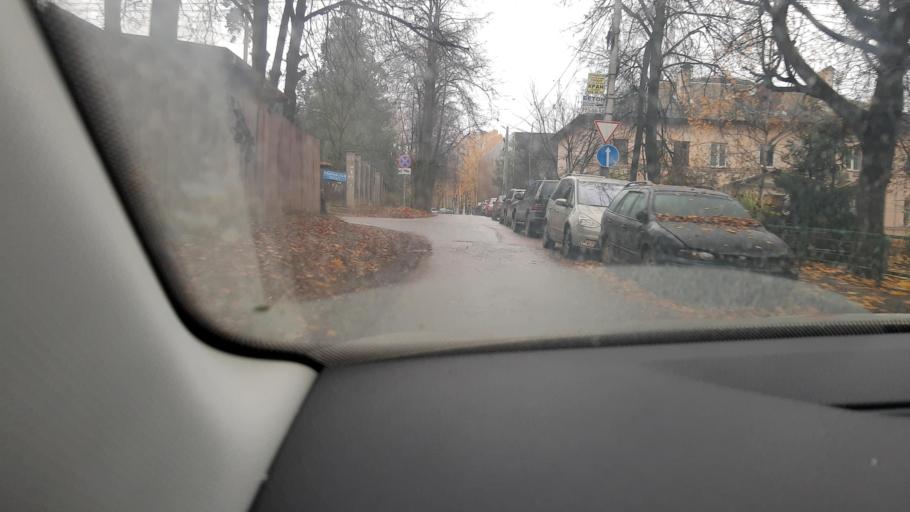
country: RU
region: Moskovskaya
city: Vidnoye
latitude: 55.5470
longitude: 37.6862
